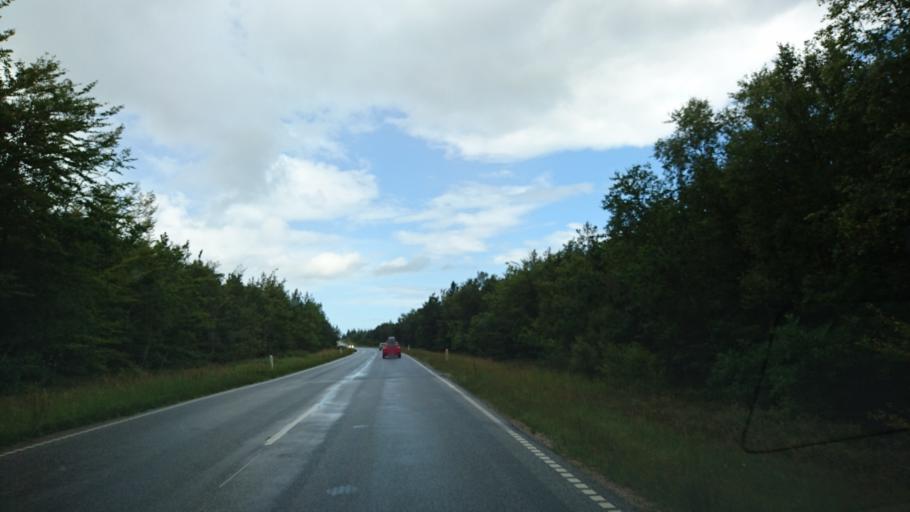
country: DK
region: North Denmark
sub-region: Frederikshavn Kommune
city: Skagen
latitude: 57.6477
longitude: 10.4611
